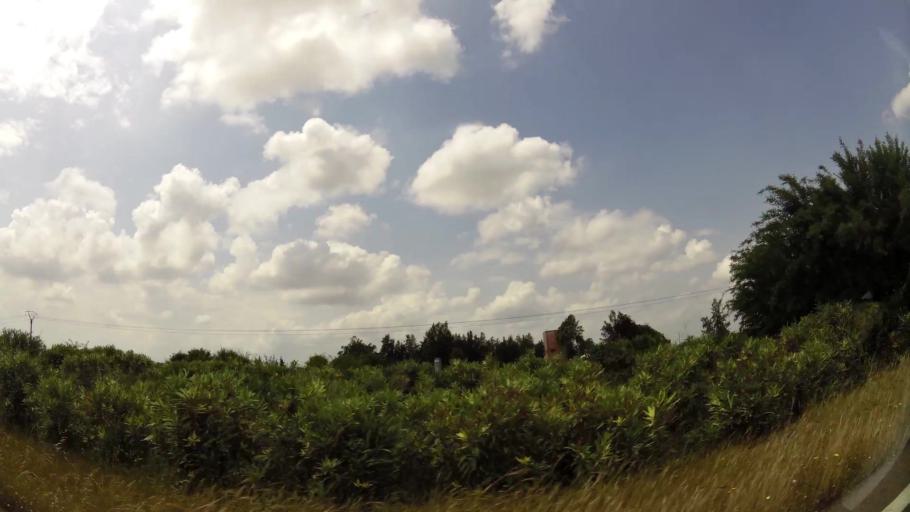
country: MA
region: Rabat-Sale-Zemmour-Zaer
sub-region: Khemisset
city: Tiflet
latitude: 33.9791
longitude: -6.5207
